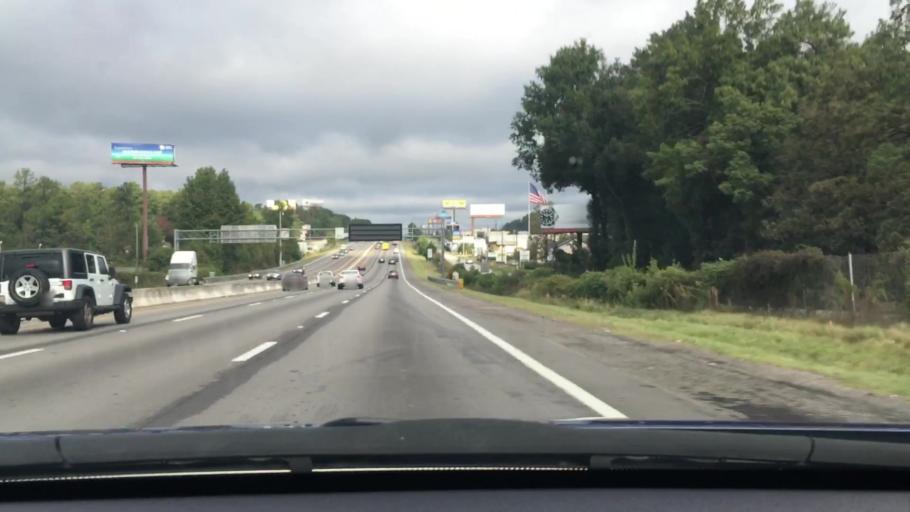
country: US
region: South Carolina
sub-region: Lexington County
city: Saint Andrews
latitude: 34.0496
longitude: -81.1230
